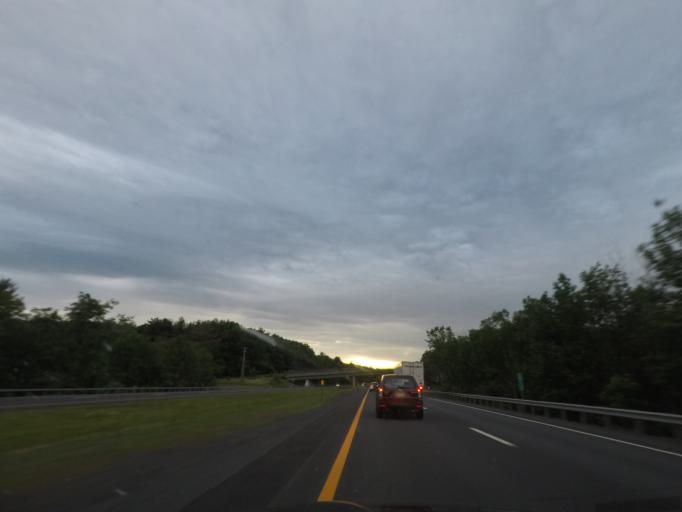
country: US
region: New York
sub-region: Rensselaer County
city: Nassau
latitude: 42.4460
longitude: -73.5646
